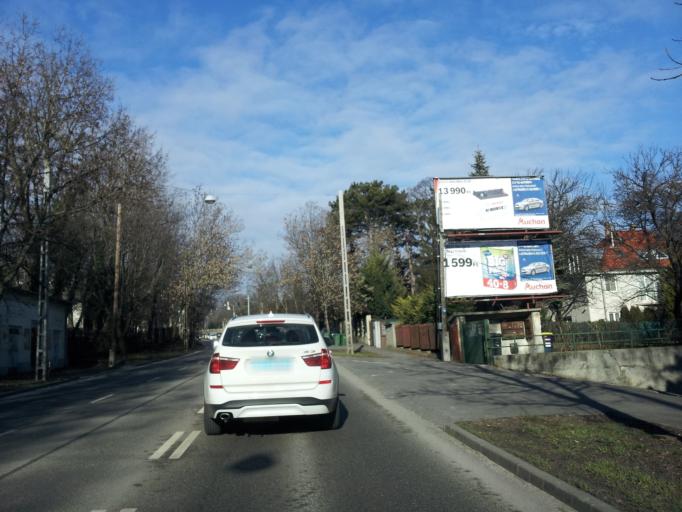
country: HU
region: Pest
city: Budakeszi
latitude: 47.5335
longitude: 18.9756
